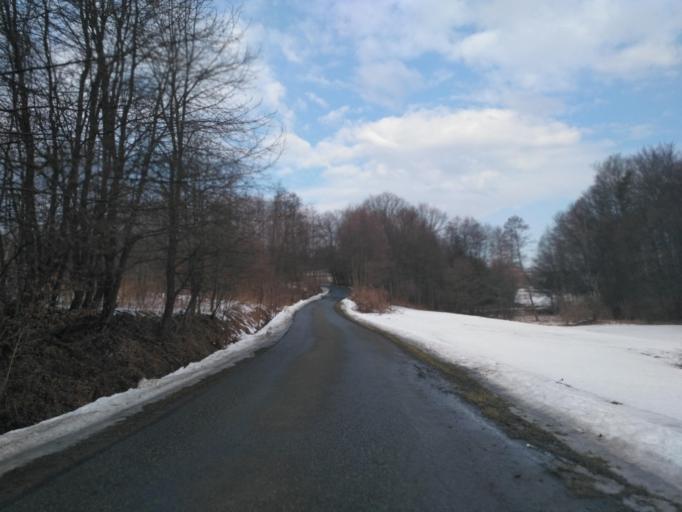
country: PL
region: Subcarpathian Voivodeship
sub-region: Powiat brzozowski
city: Niebocko
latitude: 49.6482
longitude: 22.1308
